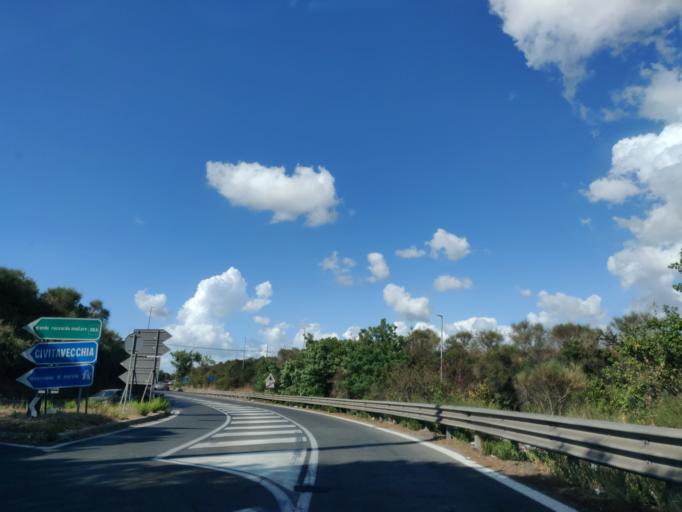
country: IT
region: Latium
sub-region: Citta metropolitana di Roma Capitale
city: La Massimina-Casal Lumbroso
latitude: 41.8862
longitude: 12.3886
